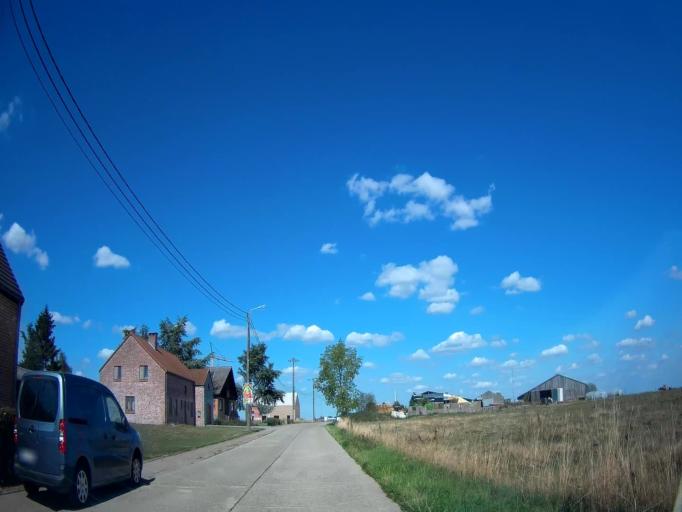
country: FR
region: Champagne-Ardenne
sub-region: Departement des Ardennes
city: Fromelennes
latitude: 50.1668
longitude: 4.8922
